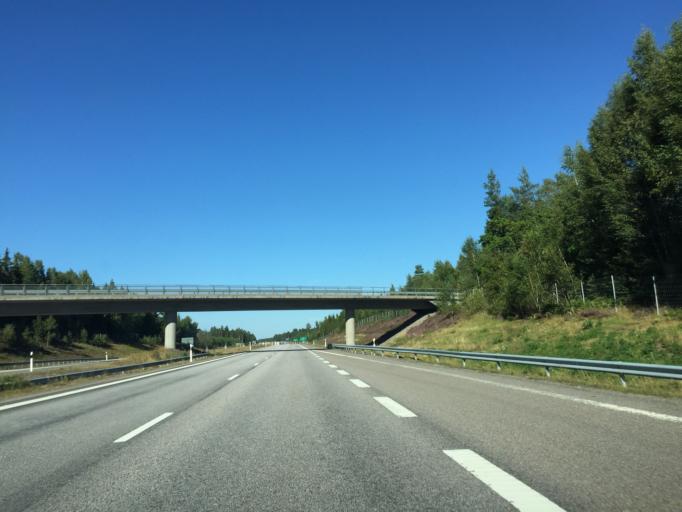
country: SE
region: OErebro
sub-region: Lindesbergs Kommun
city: Fellingsbro
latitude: 59.3443
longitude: 15.5484
